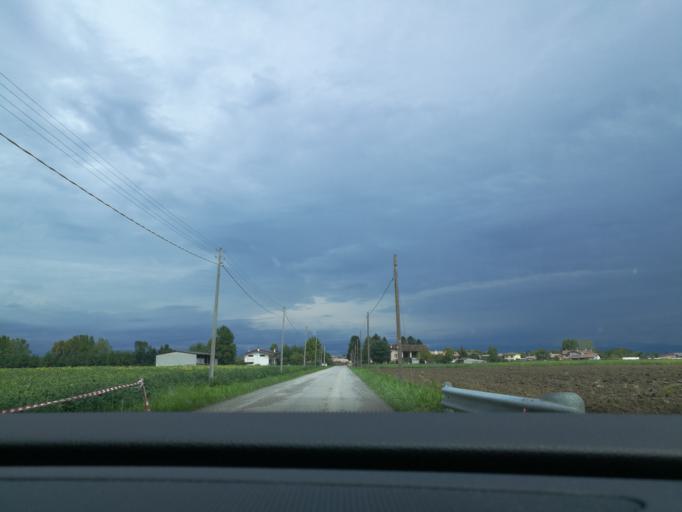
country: IT
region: Friuli Venezia Giulia
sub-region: Provincia di Udine
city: Porpetto
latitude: 45.8511
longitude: 13.1826
